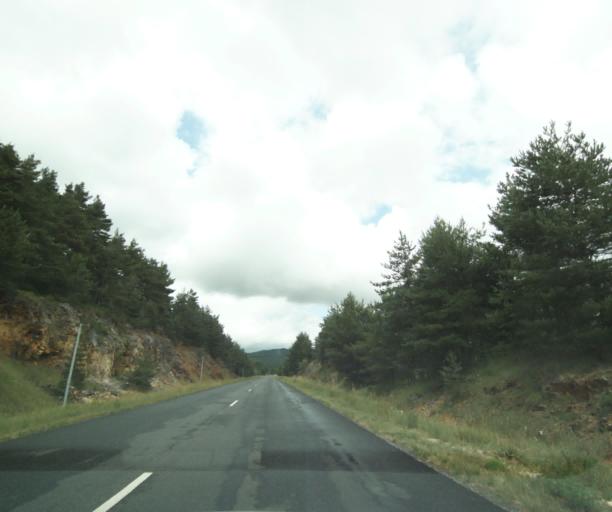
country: FR
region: Midi-Pyrenees
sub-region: Departement de l'Aveyron
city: Severac-le-Chateau
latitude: 44.3762
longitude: 3.1137
